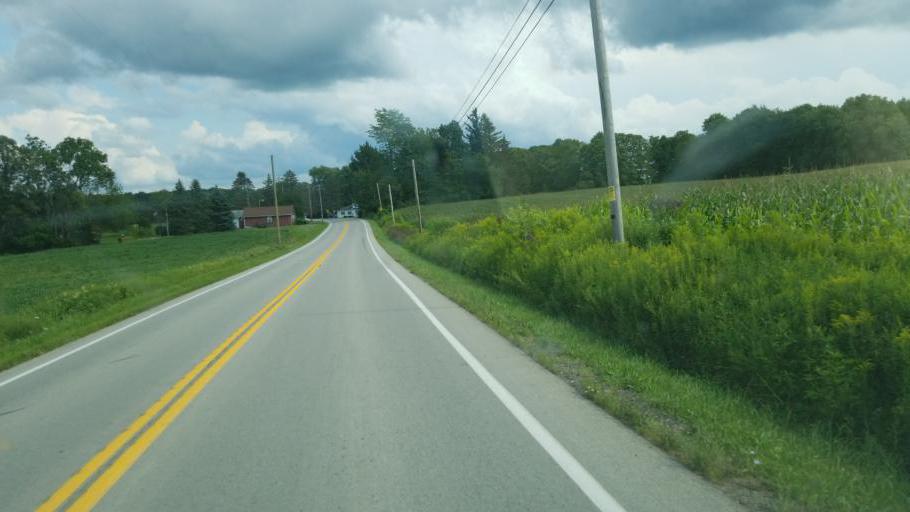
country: US
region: Pennsylvania
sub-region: Crawford County
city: Conneaut Lakeshore
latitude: 41.5707
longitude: -80.2820
